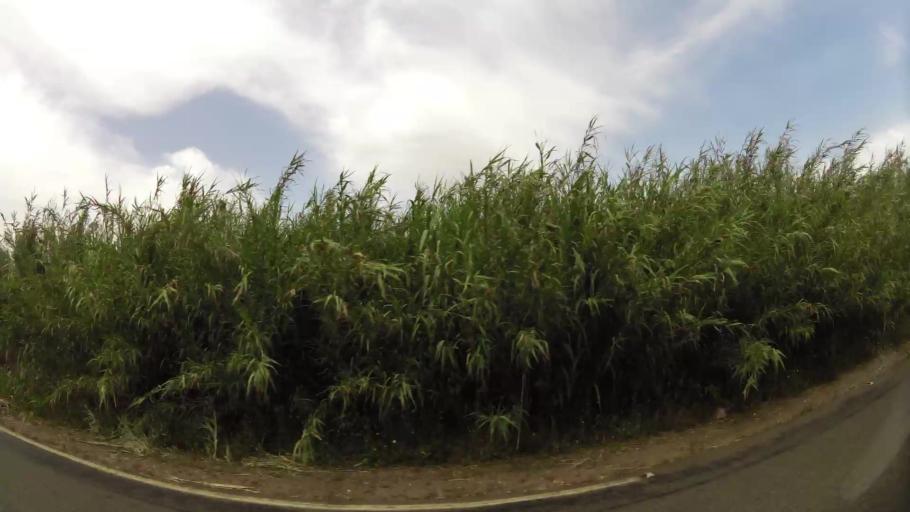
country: MA
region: Rabat-Sale-Zemmour-Zaer
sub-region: Khemisset
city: Khemisset
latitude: 33.7532
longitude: -6.1984
